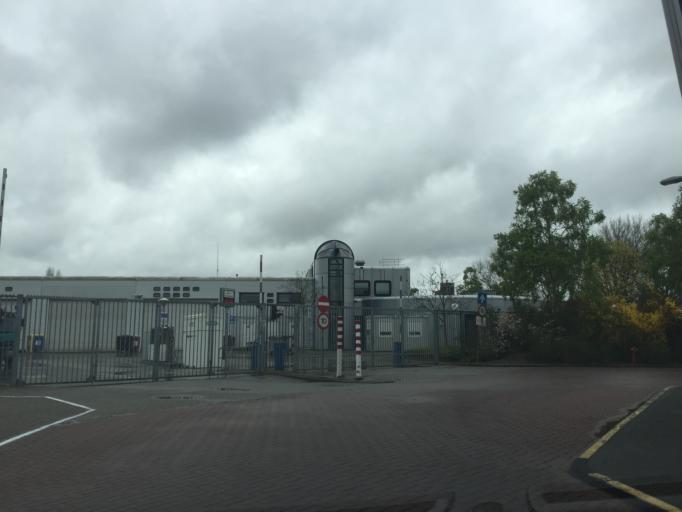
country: NL
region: South Holland
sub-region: Gemeente Leiderdorp
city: Leiderdorp
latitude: 52.1568
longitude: 4.5116
